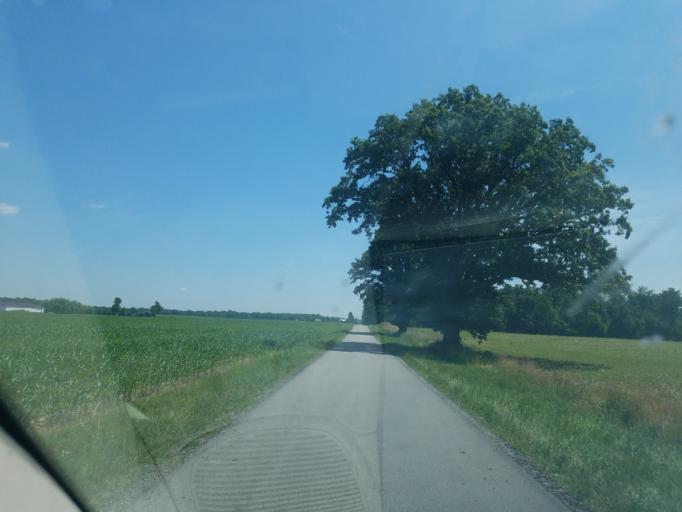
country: US
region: Ohio
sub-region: Hancock County
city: Arlington
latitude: 40.8558
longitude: -83.7074
